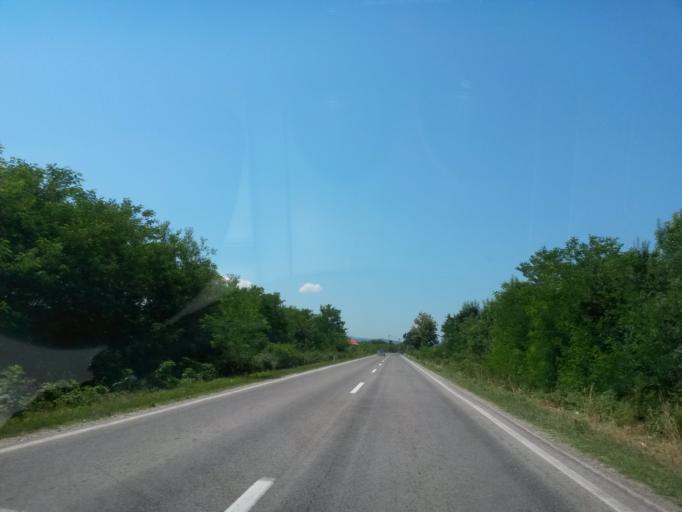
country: BA
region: Federation of Bosnia and Herzegovina
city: Odzak
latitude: 44.9828
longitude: 18.3736
